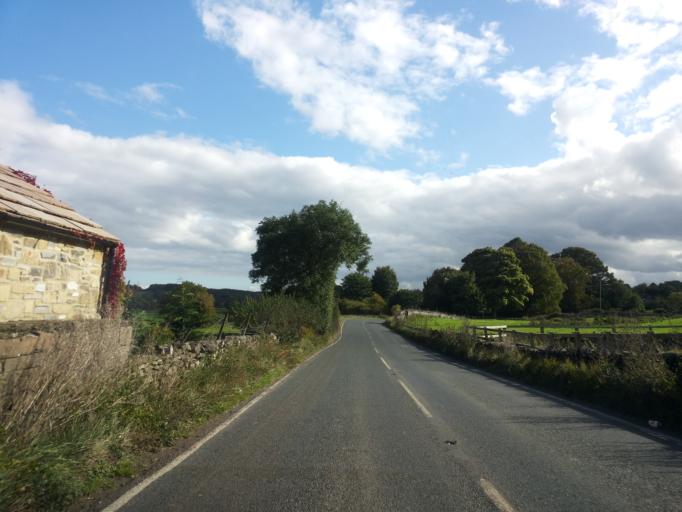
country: GB
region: England
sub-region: North Yorkshire
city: Leyburn
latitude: 54.2925
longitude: -1.8166
